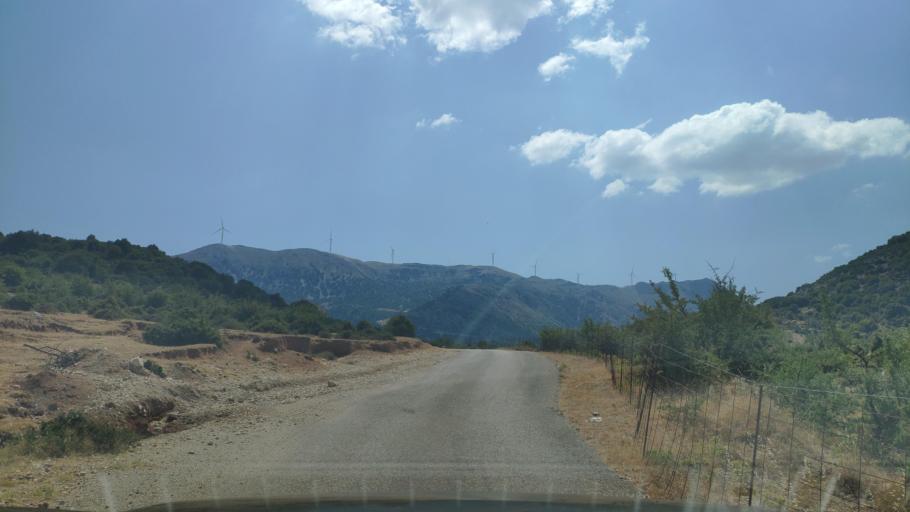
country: GR
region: West Greece
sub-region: Nomos Aitolias kai Akarnanias
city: Monastirakion
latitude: 38.7970
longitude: 20.9549
